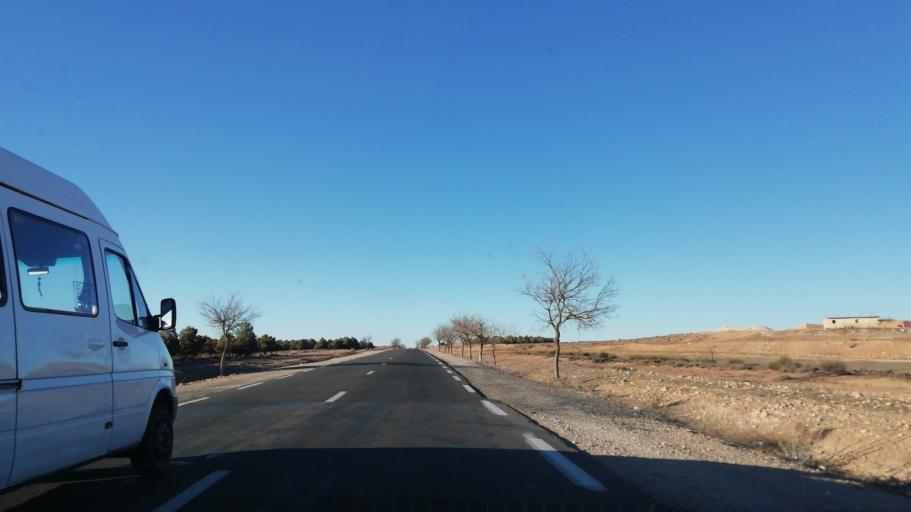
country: DZ
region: Tlemcen
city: Sebdou
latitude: 34.5267
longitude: -1.2927
